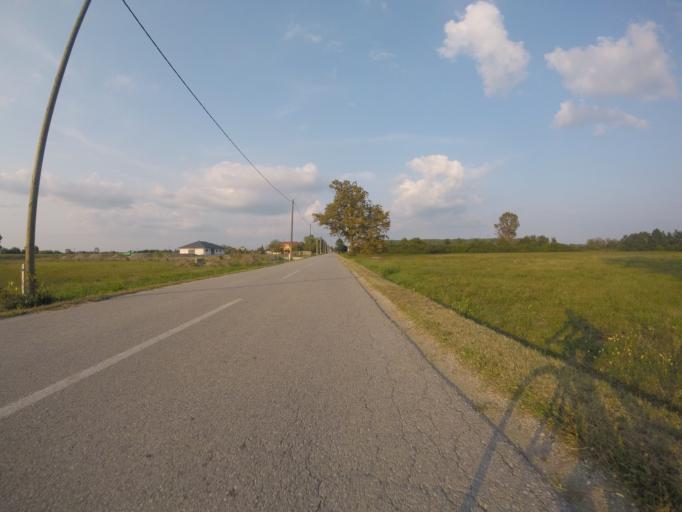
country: HR
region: Zagrebacka
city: Kuce
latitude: 45.7182
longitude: 16.1995
